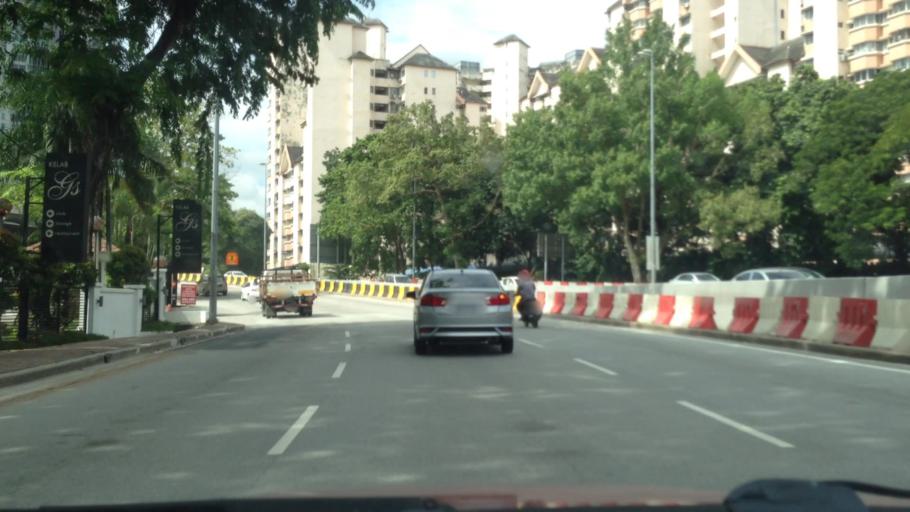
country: MY
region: Kuala Lumpur
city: Kuala Lumpur
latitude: 3.0883
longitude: 101.6932
